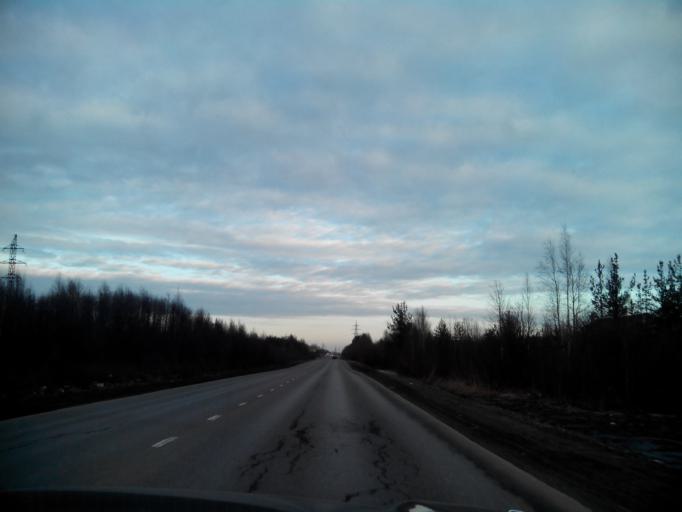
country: RU
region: Arkhangelskaya
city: Arkhangel'sk
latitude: 64.5236
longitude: 40.6673
